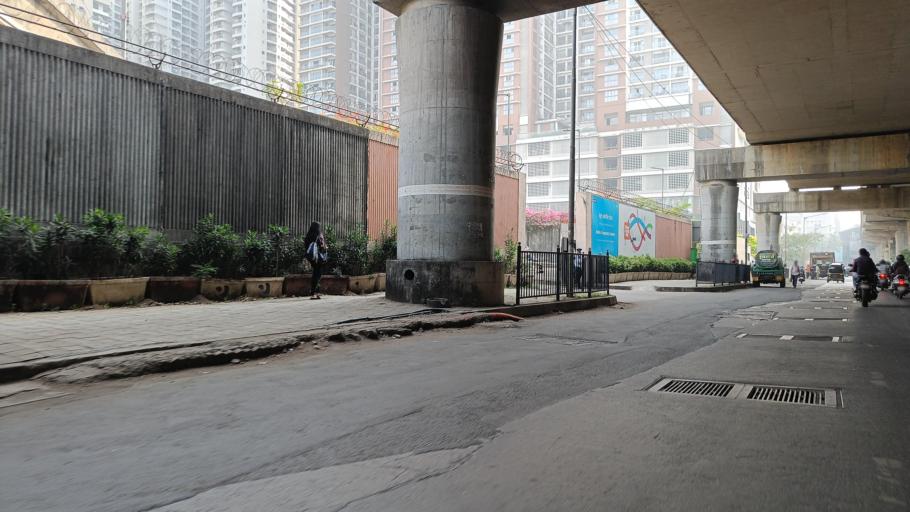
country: IN
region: Maharashtra
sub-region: Mumbai Suburban
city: Powai
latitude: 19.1290
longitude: 72.8262
